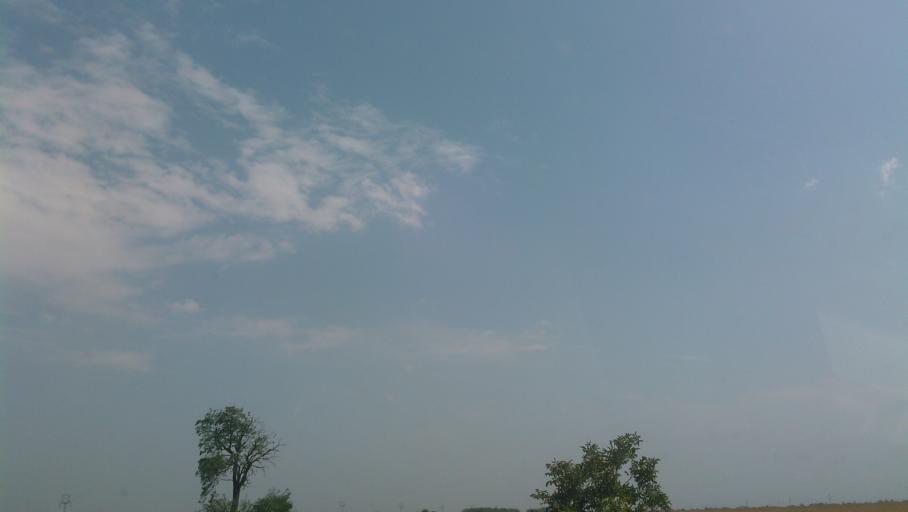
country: SK
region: Trnavsky
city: Samorin
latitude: 48.0943
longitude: 17.3638
